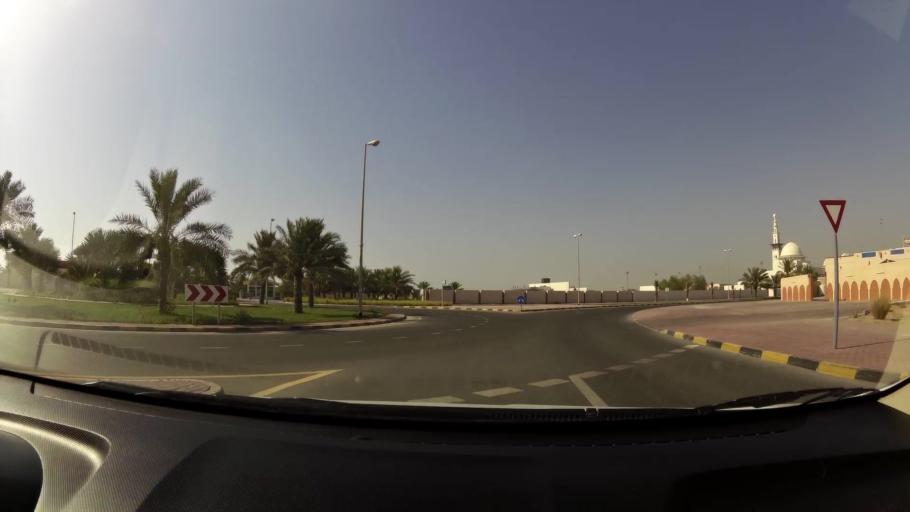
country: AE
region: Ajman
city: Ajman
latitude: 25.4205
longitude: 55.4645
